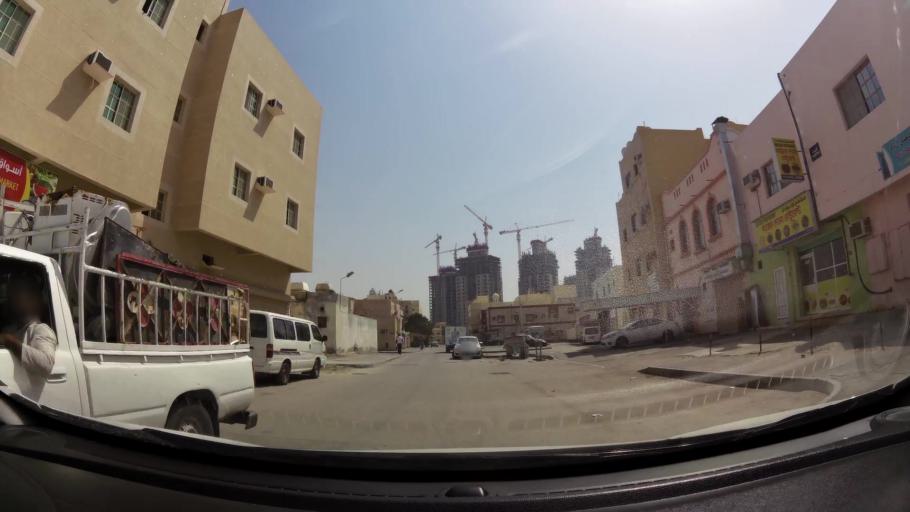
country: BH
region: Manama
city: Jidd Hafs
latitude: 26.2080
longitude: 50.4508
